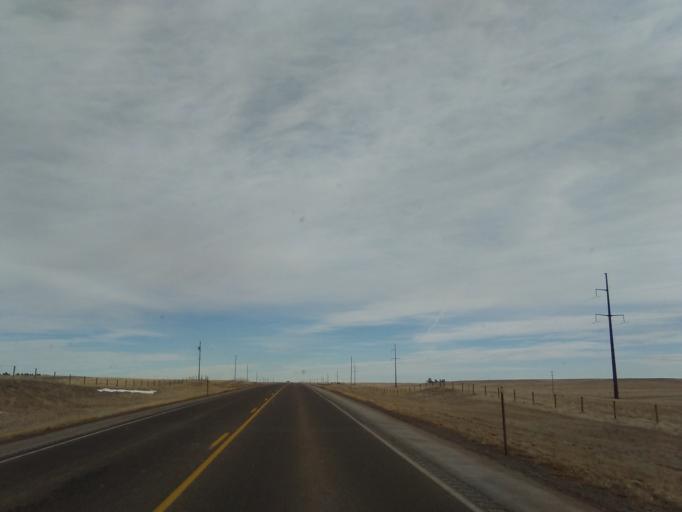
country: US
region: Wyoming
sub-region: Laramie County
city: Ranchettes
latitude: 41.3646
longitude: -104.5778
